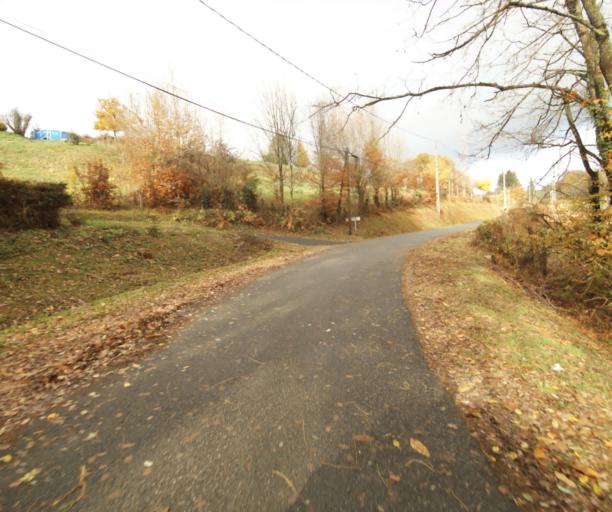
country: FR
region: Limousin
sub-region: Departement de la Correze
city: Sainte-Fereole
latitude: 45.2177
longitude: 1.6247
